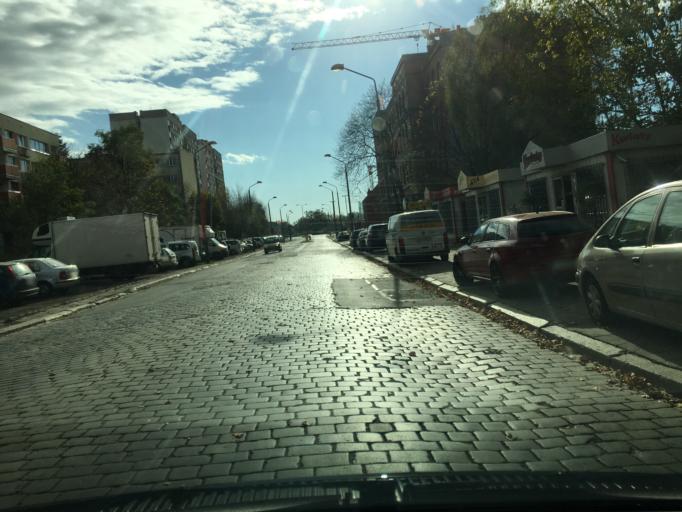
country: PL
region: Lower Silesian Voivodeship
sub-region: Powiat wroclawski
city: Wroclaw
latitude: 51.1156
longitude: 17.0066
